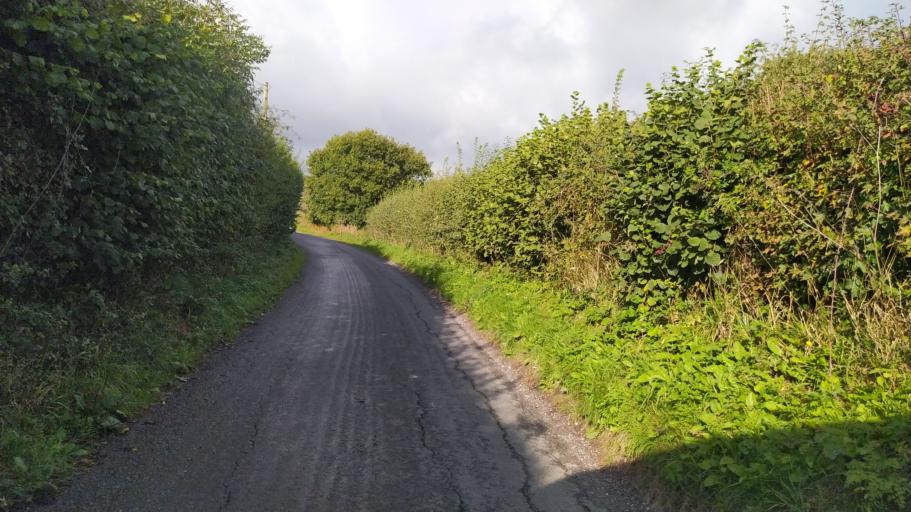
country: GB
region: England
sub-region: Dorset
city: Shaftesbury
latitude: 51.0394
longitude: -2.1480
